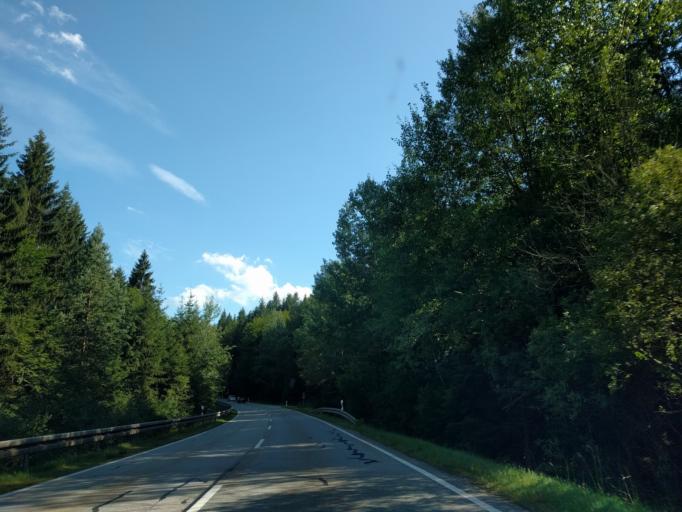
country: DE
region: Bavaria
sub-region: Lower Bavaria
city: Bodenmais
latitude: 49.0423
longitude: 13.1156
